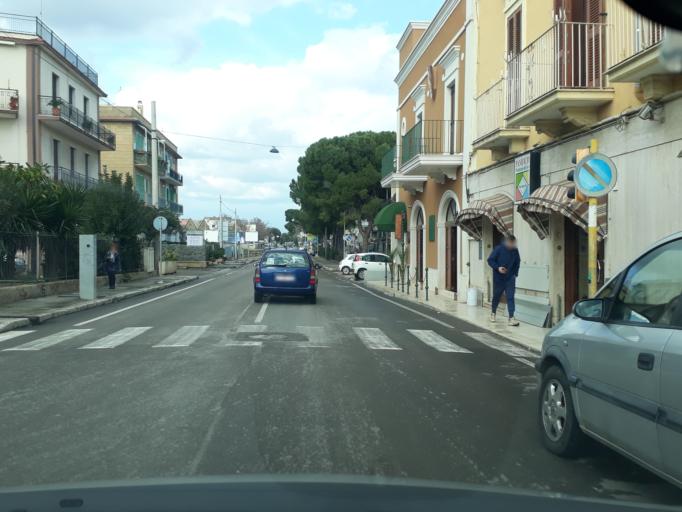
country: IT
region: Apulia
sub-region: Provincia di Brindisi
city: Fasano
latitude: 40.8395
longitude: 17.3595
